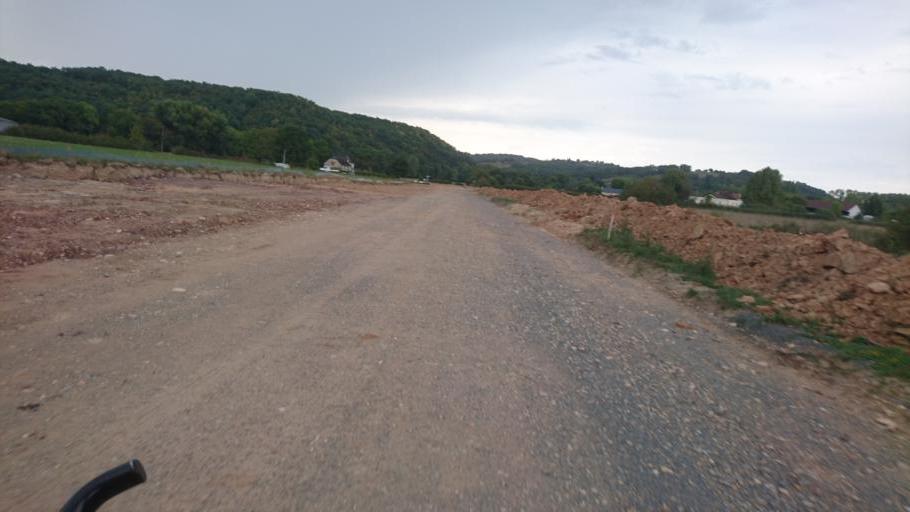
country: FR
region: Limousin
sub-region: Departement de la Correze
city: Saint-Pantaleon-de-Larche
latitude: 45.1565
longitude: 1.4648
